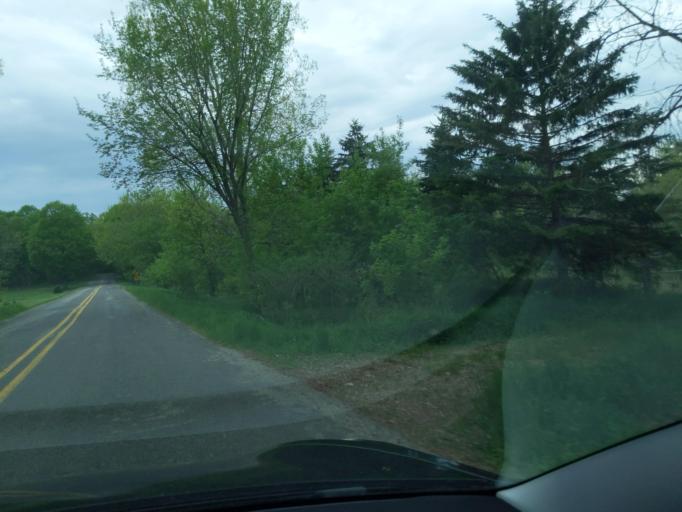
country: US
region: Michigan
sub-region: Ingham County
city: Stockbridge
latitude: 42.5125
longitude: -84.2757
